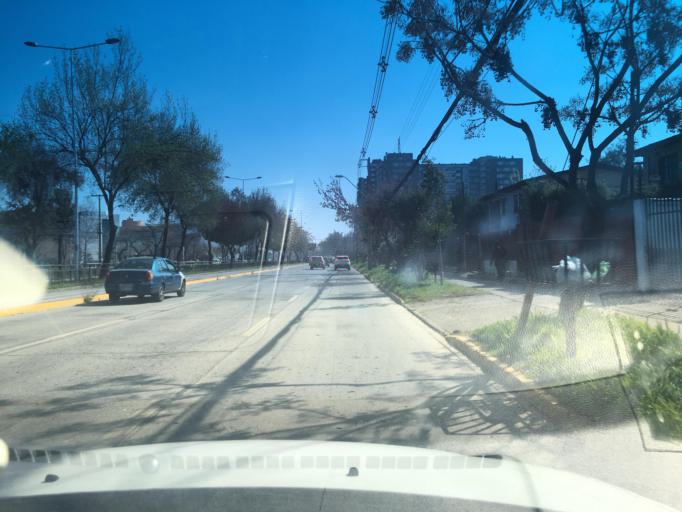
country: CL
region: Santiago Metropolitan
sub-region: Provincia de Santiago
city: Villa Presidente Frei, Nunoa, Santiago, Chile
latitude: -33.4649
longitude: -70.5919
